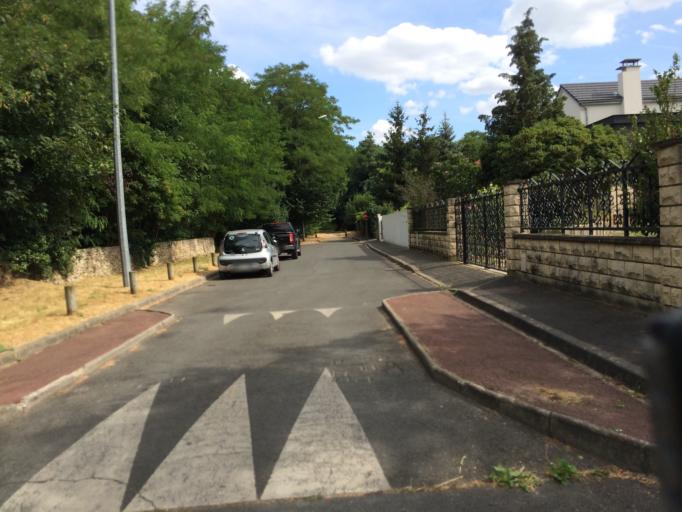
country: FR
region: Ile-de-France
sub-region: Departement de l'Essonne
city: Draveil
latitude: 48.6809
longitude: 2.4349
